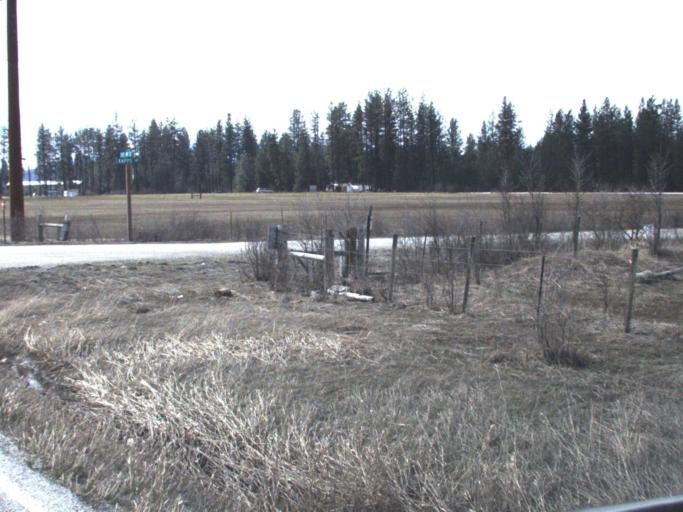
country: US
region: Washington
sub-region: Pend Oreille County
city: Newport
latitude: 48.3458
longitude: -117.3045
